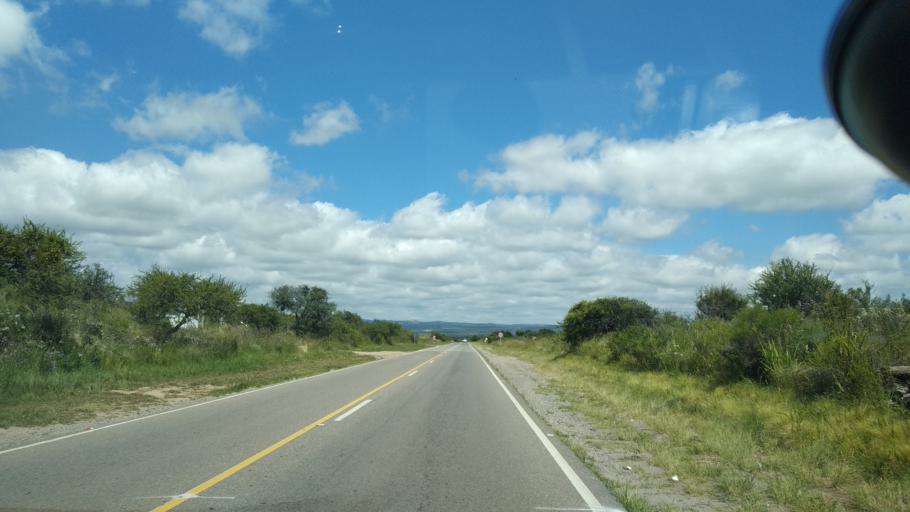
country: AR
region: Cordoba
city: Villa Cura Brochero
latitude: -31.6937
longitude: -65.0619
